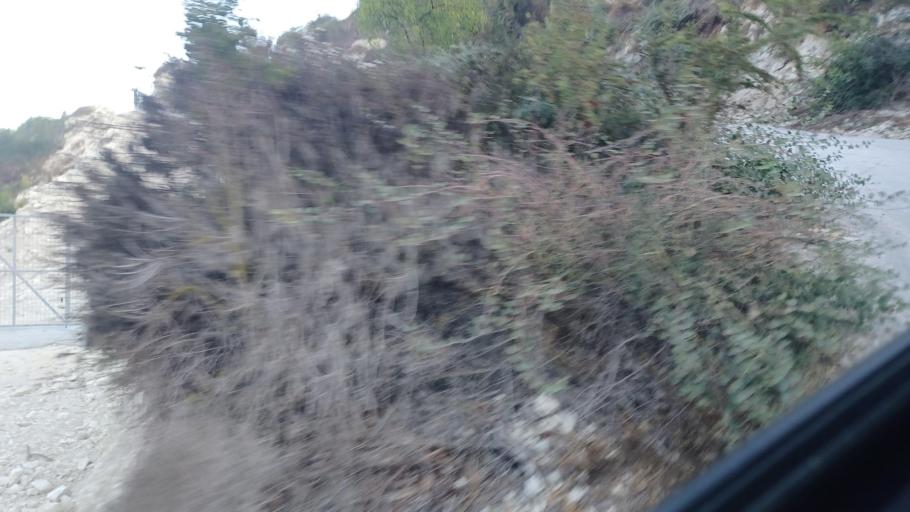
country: CY
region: Pafos
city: Tala
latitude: 34.8626
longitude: 32.4650
